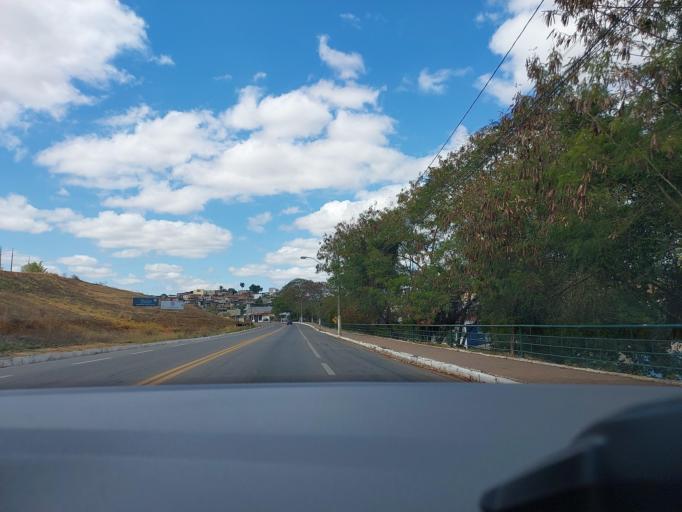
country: BR
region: Minas Gerais
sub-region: Muriae
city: Muriae
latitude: -21.1287
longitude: -42.3624
